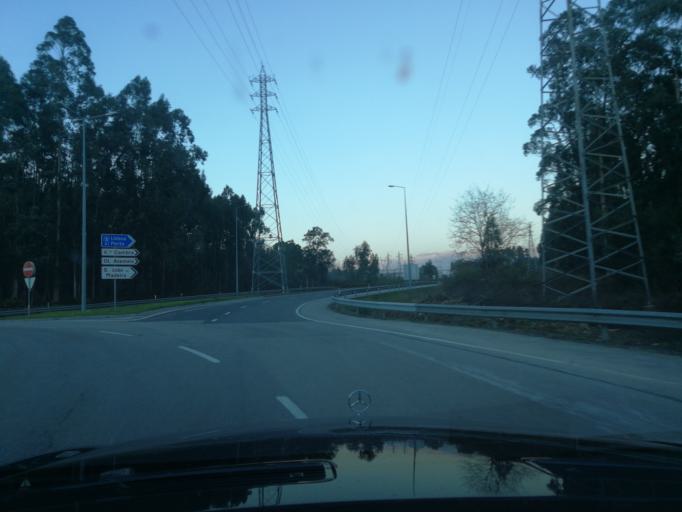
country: PT
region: Aveiro
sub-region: Estarreja
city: Beduido
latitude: 40.7835
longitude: -8.5594
